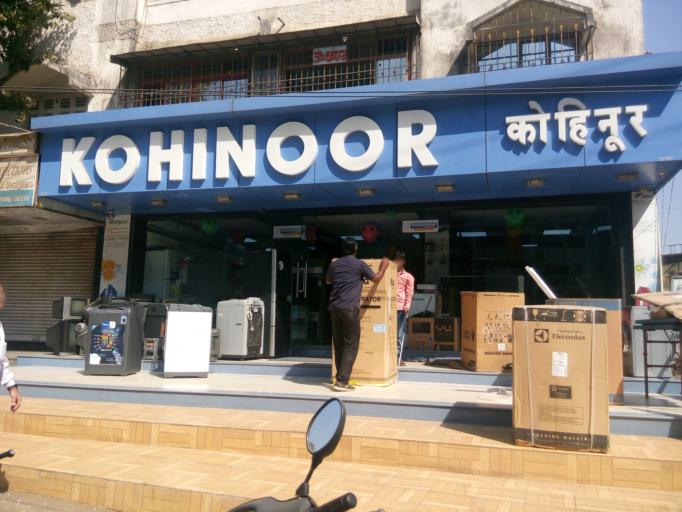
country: IN
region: Maharashtra
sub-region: Thane
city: Dombivli
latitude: 19.2118
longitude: 73.0927
